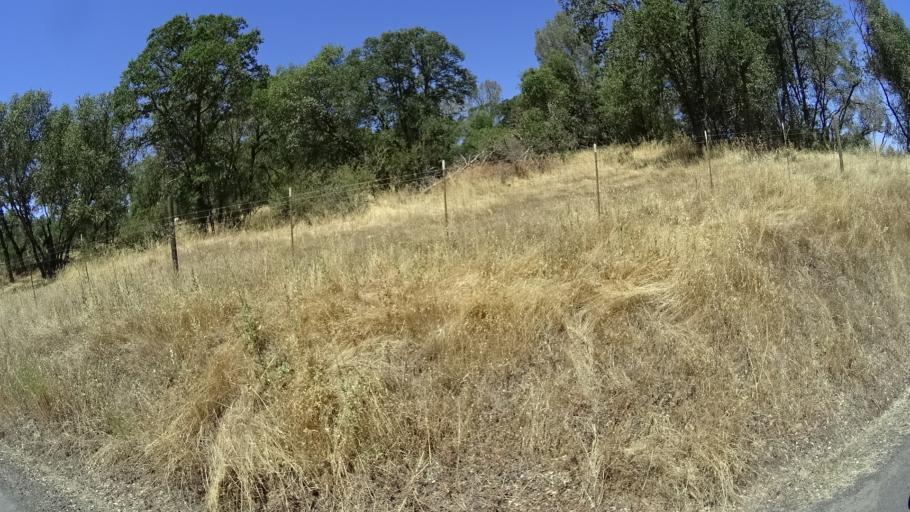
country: US
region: California
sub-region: Calaveras County
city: Copperopolis
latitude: 37.9897
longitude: -120.7011
